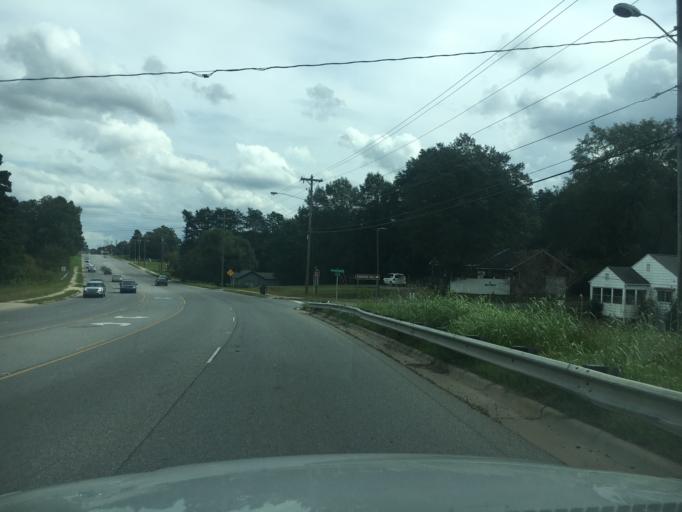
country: US
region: North Carolina
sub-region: Gaston County
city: Bessemer City
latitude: 35.2825
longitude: -81.2391
